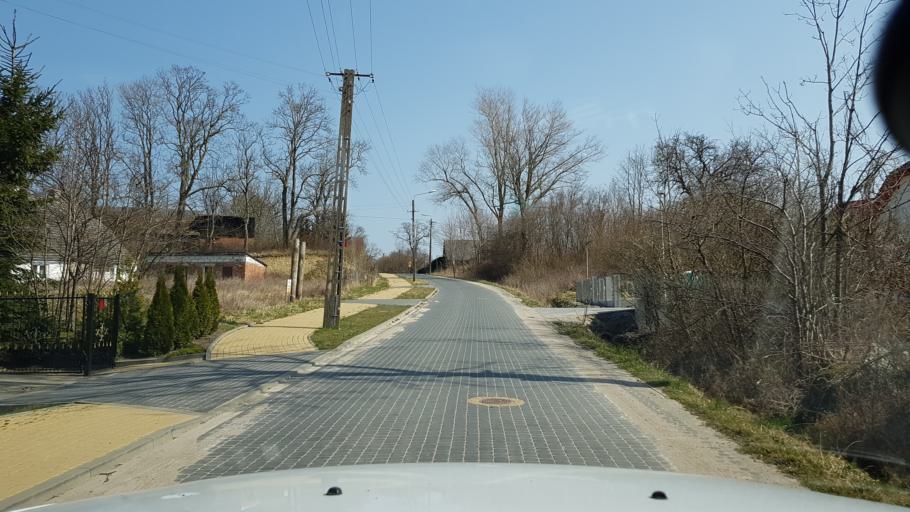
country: PL
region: West Pomeranian Voivodeship
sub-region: Powiat slawienski
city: Darlowo
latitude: 54.5078
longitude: 16.5032
